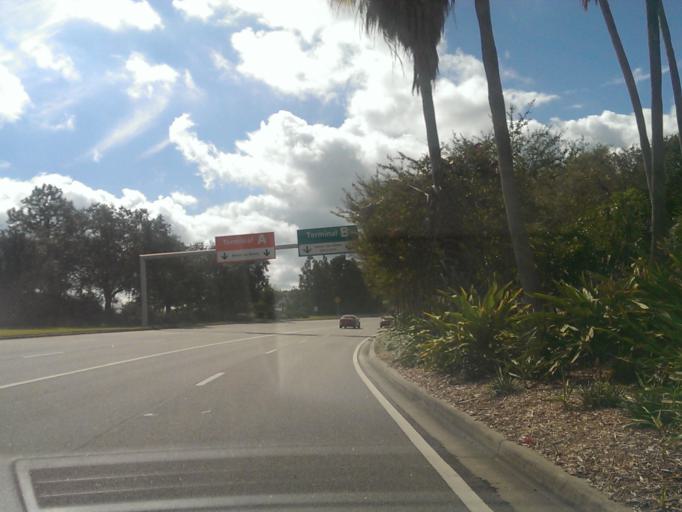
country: US
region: Florida
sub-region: Orange County
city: Belle Isle
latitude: 28.4379
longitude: -81.3106
